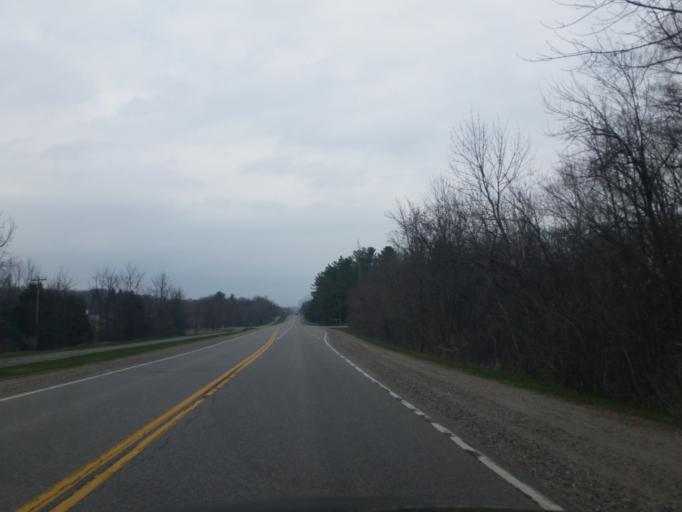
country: US
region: New York
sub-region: Jefferson County
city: Alexandria Bay
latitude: 44.3823
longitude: -75.9341
